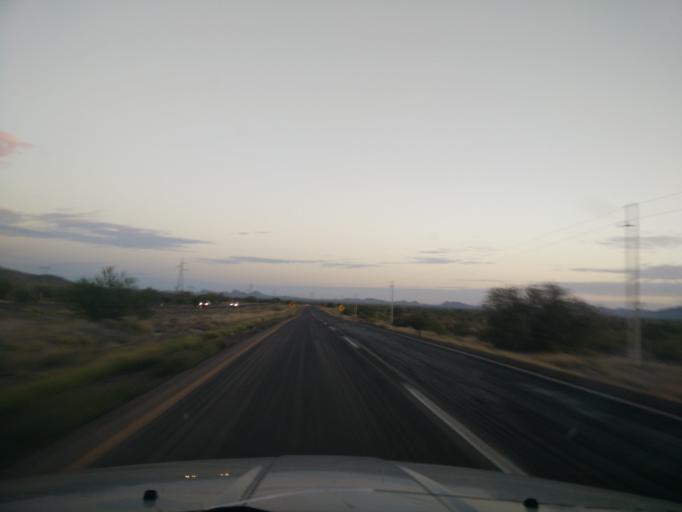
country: MX
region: Sonora
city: Heroica Guaymas
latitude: 28.2790
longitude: -111.0390
